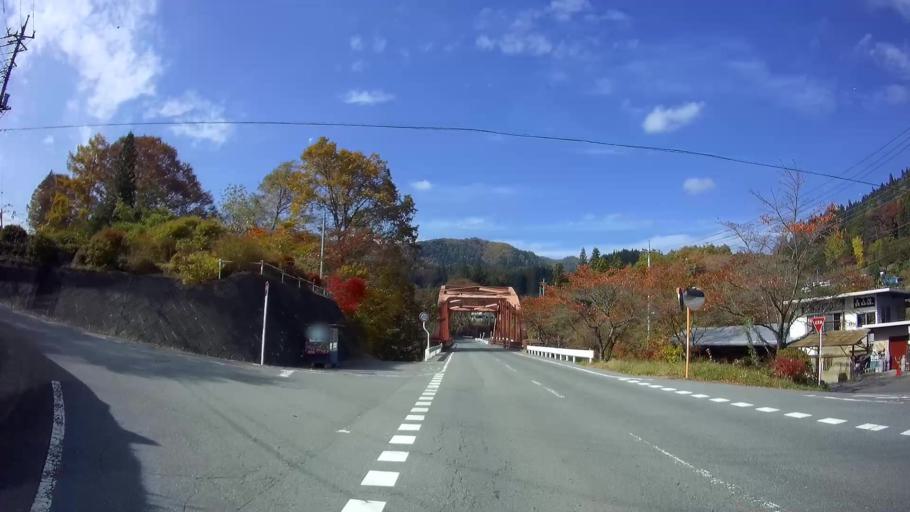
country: JP
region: Gunma
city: Nakanojomachi
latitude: 36.5064
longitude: 138.7142
